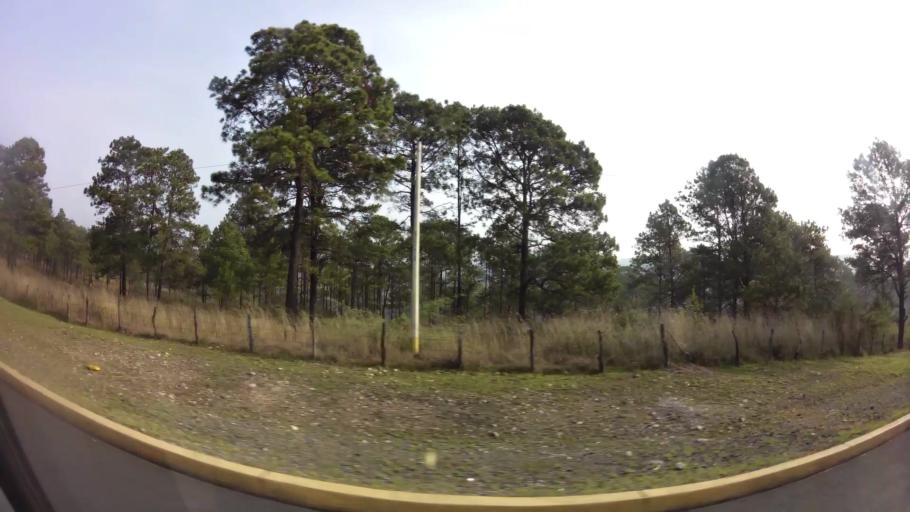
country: HN
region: Francisco Morazan
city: Zambrano
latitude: 14.2515
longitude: -87.3798
